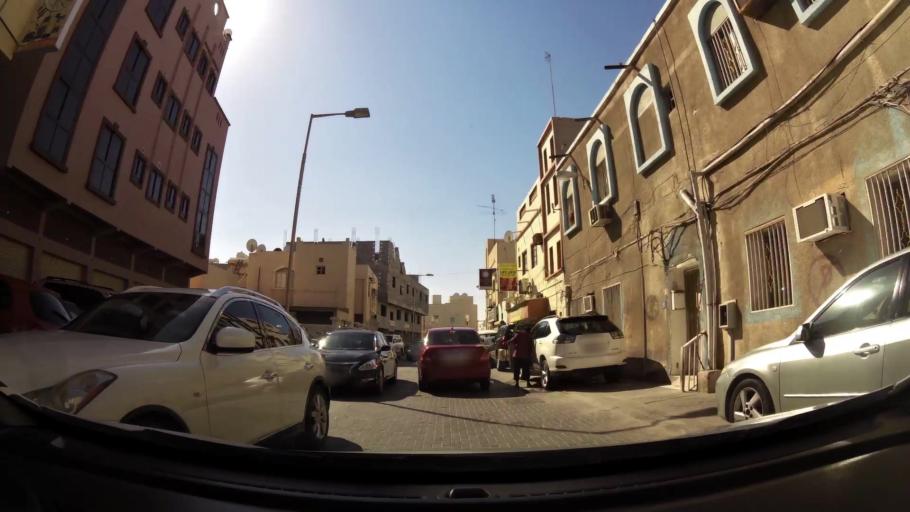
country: BH
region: Muharraq
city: Al Hadd
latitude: 26.2421
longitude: 50.6542
